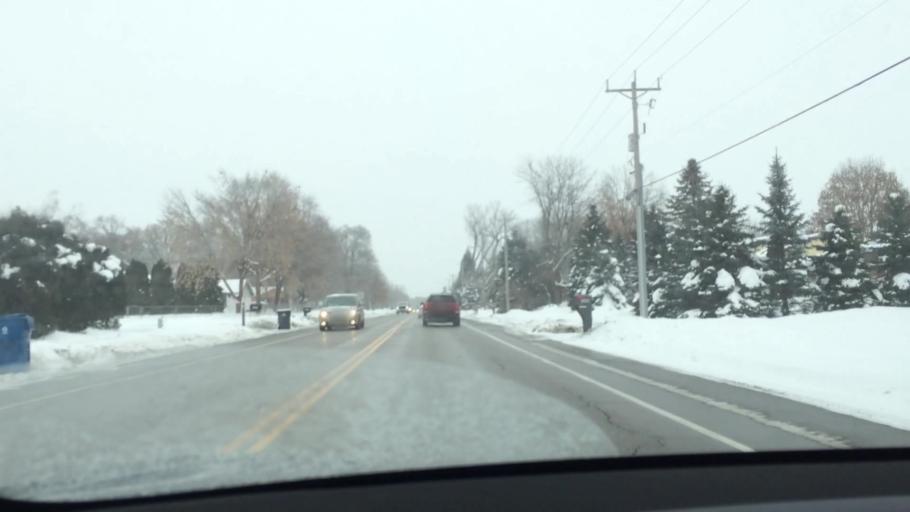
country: US
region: Minnesota
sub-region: Anoka County
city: Circle Pines
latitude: 45.1179
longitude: -93.1274
